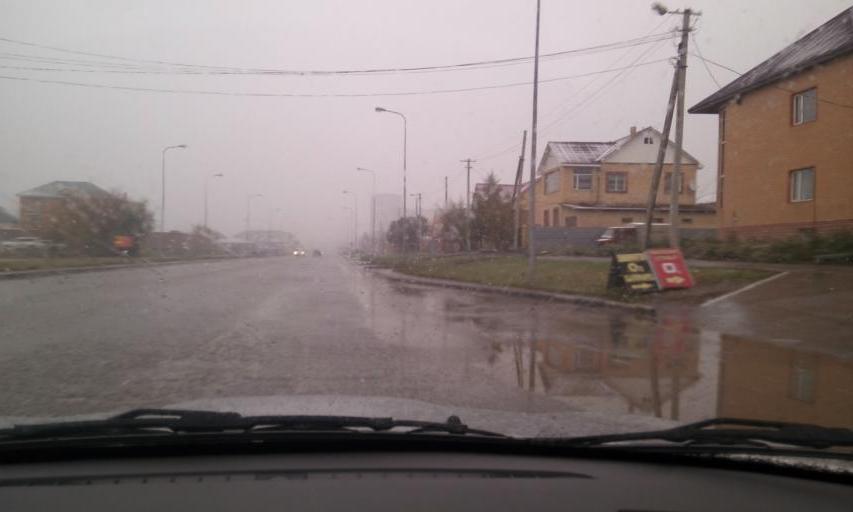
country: KZ
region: Astana Qalasy
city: Astana
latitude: 51.1760
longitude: 71.3671
